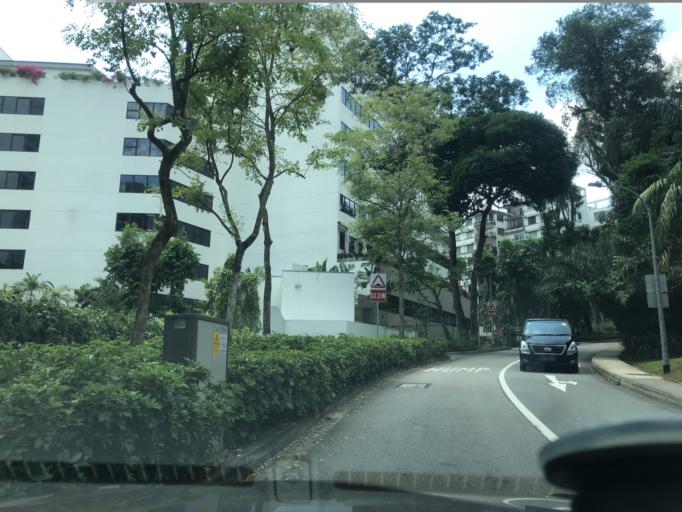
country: SG
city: Singapore
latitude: 1.3071
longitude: 103.8210
